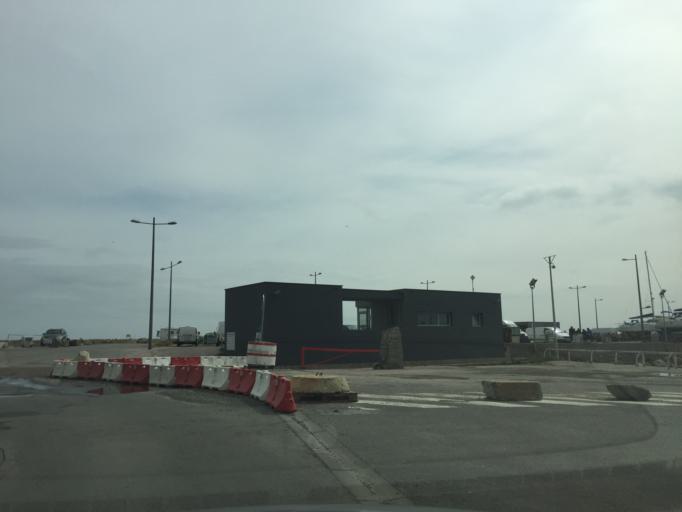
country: FR
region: Brittany
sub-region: Departement des Cotes-d'Armor
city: Saint-Cast-le-Guildo
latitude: 48.6415
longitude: -2.2456
